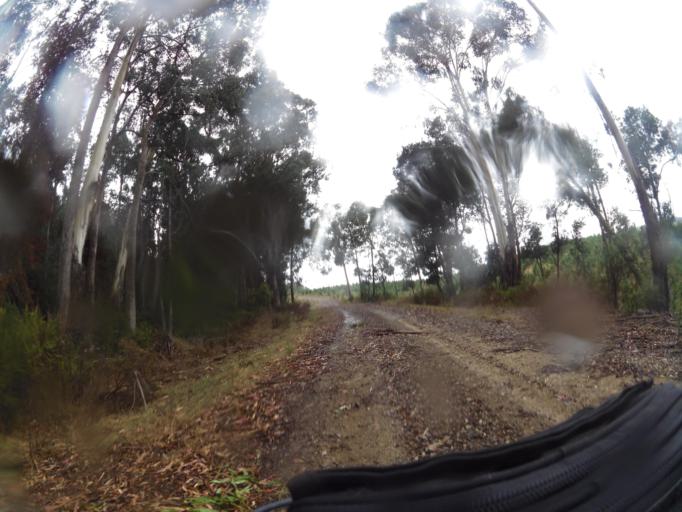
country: AU
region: New South Wales
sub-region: Greater Hume Shire
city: Holbrook
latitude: -36.2177
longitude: 147.5663
